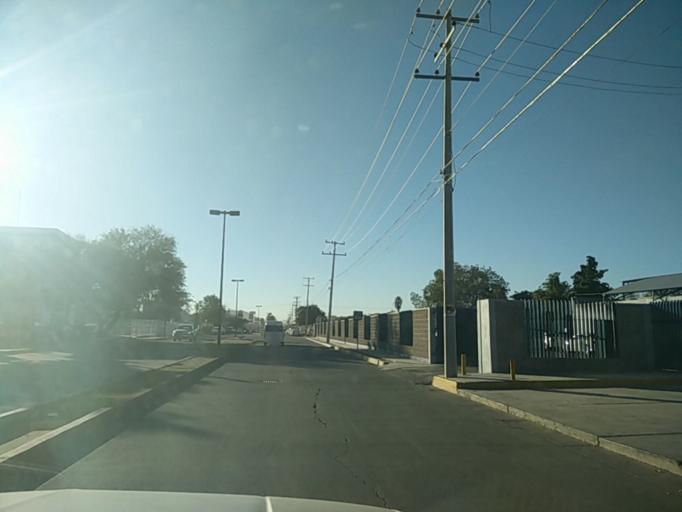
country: MX
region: Sonora
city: Hermosillo
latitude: 29.0825
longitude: -111.0006
